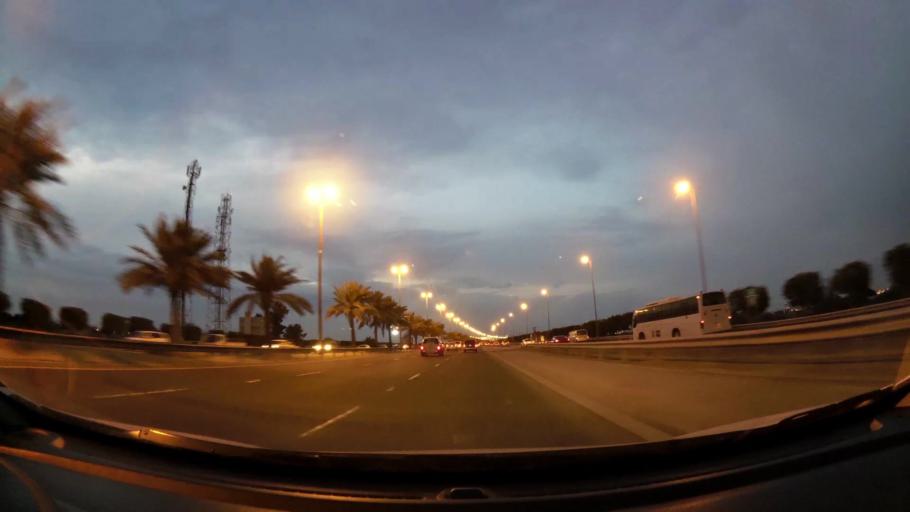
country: BH
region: Northern
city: Madinat `Isa
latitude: 26.1660
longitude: 50.5035
